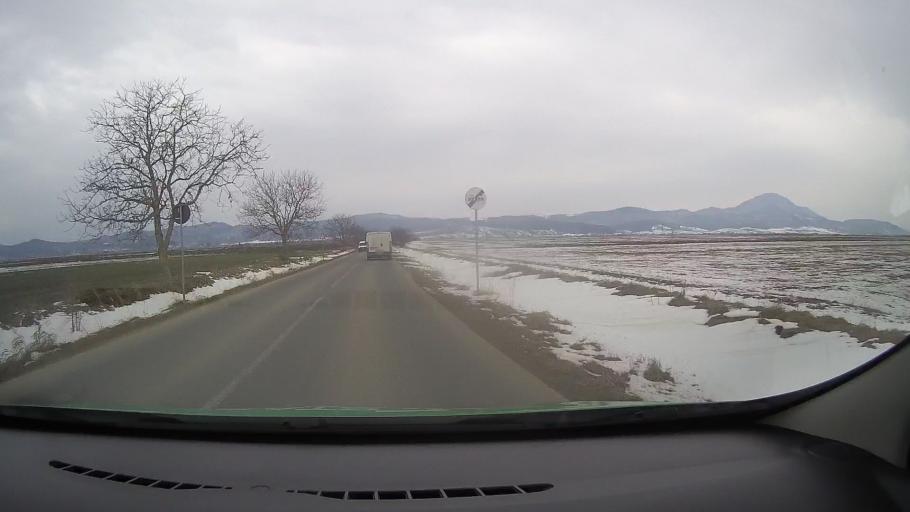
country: RO
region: Brasov
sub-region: Comuna Cristian
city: Cristian
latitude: 45.6342
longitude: 25.4534
